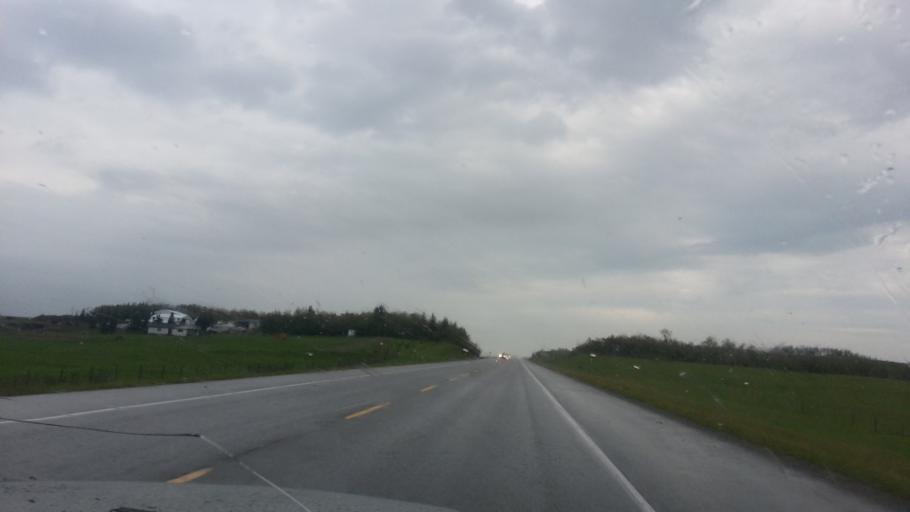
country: CA
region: Alberta
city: Cochrane
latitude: 51.0490
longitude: -114.4667
